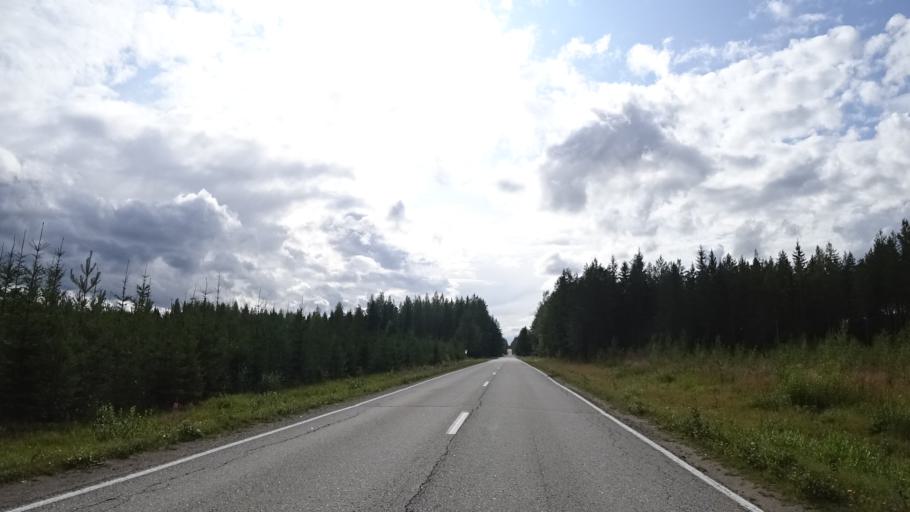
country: FI
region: North Karelia
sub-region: Joensuu
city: Ilomantsi
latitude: 62.7607
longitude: 31.0175
